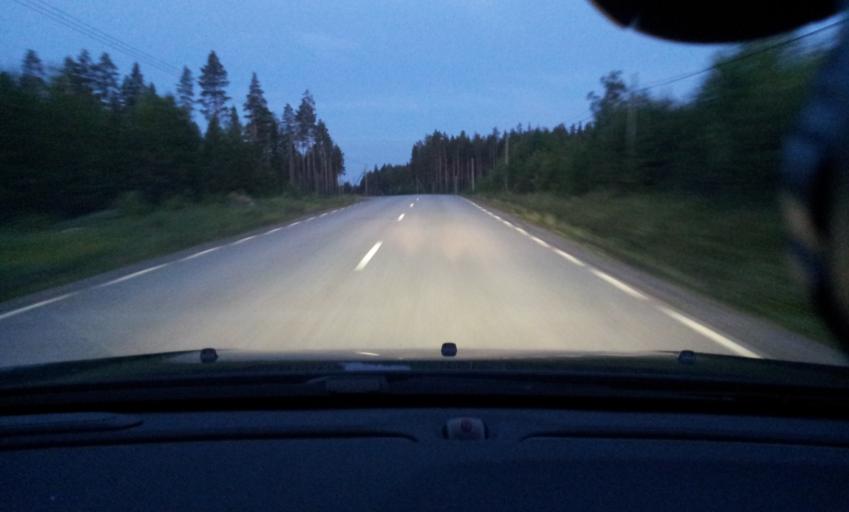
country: SE
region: Jaemtland
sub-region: OEstersunds Kommun
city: Brunflo
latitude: 62.7077
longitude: 14.9582
